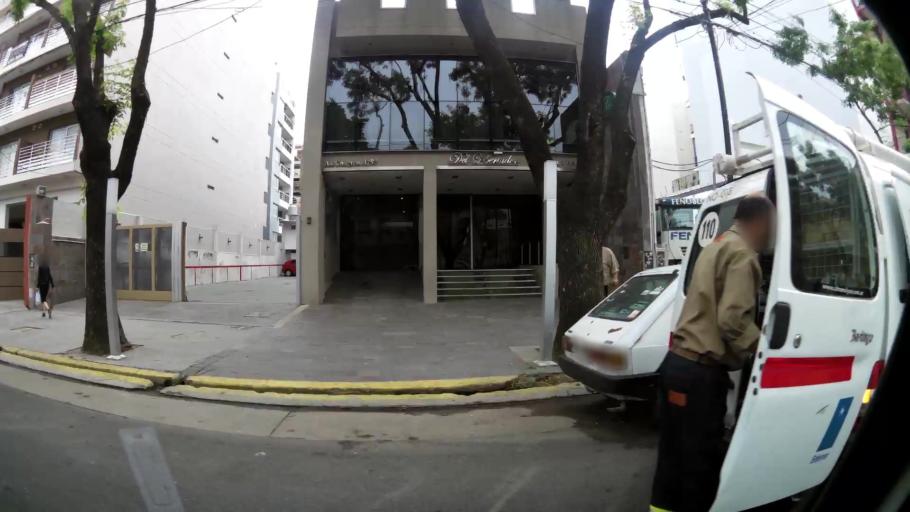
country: AR
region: Buenos Aires F.D.
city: Colegiales
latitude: -34.5520
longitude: -58.4561
